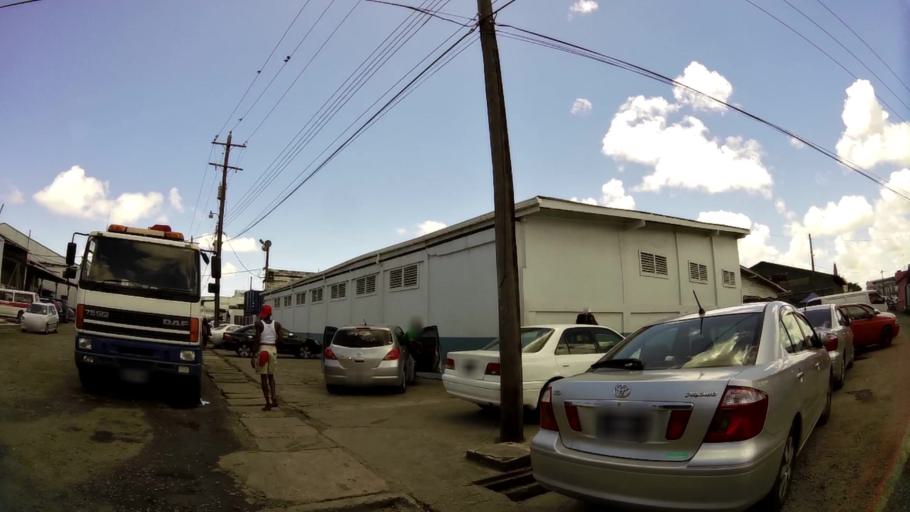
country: GY
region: Demerara-Mahaica
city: Georgetown
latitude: 6.8116
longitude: -58.1677
